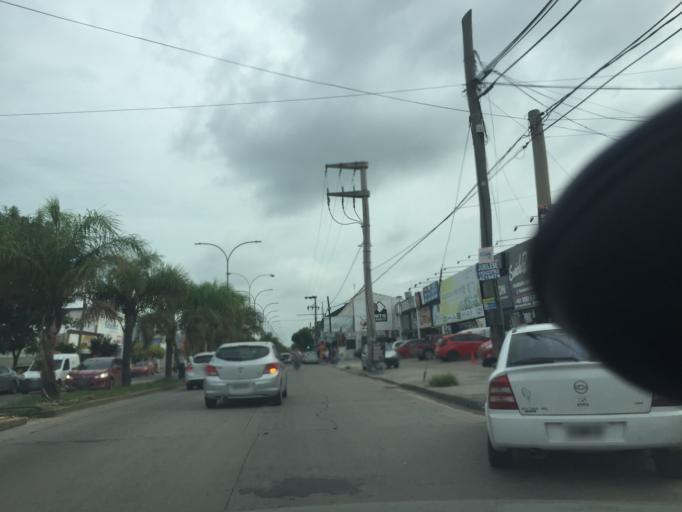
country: AR
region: Cordoba
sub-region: Departamento de Capital
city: Cordoba
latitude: -31.4463
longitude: -64.1986
